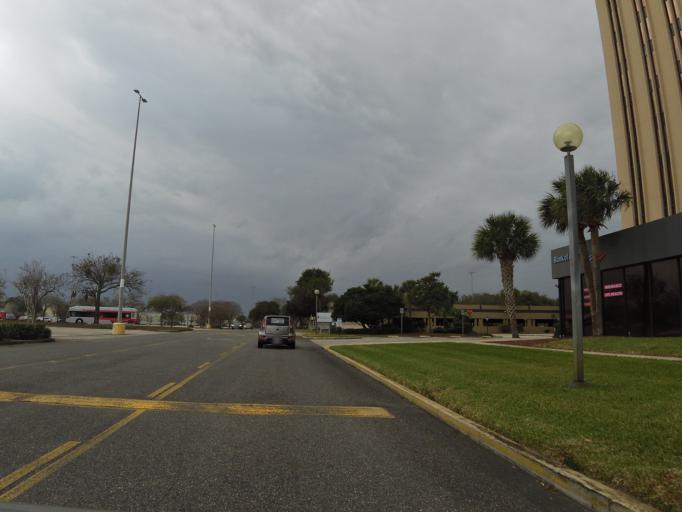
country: US
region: Florida
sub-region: Duval County
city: Jacksonville
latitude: 30.3252
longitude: -81.5498
